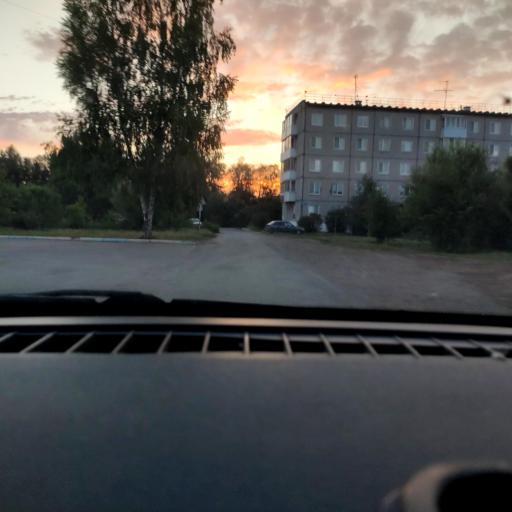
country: RU
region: Perm
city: Kukushtan
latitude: 57.6341
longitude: 56.5276
